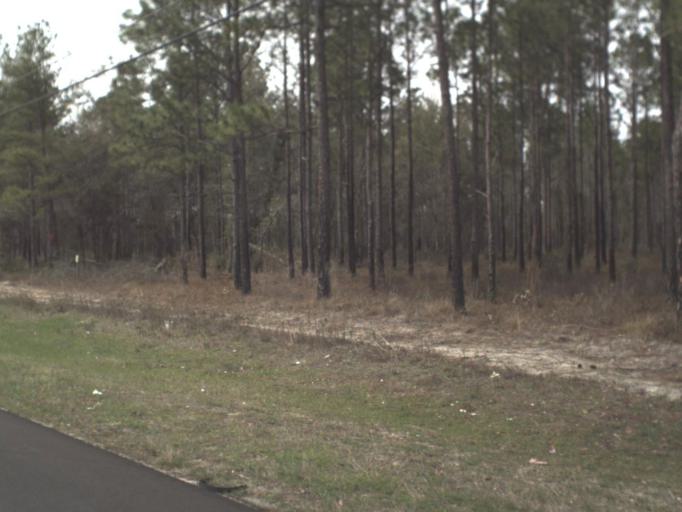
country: US
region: Florida
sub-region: Gadsden County
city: Midway
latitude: 30.4418
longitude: -84.4331
